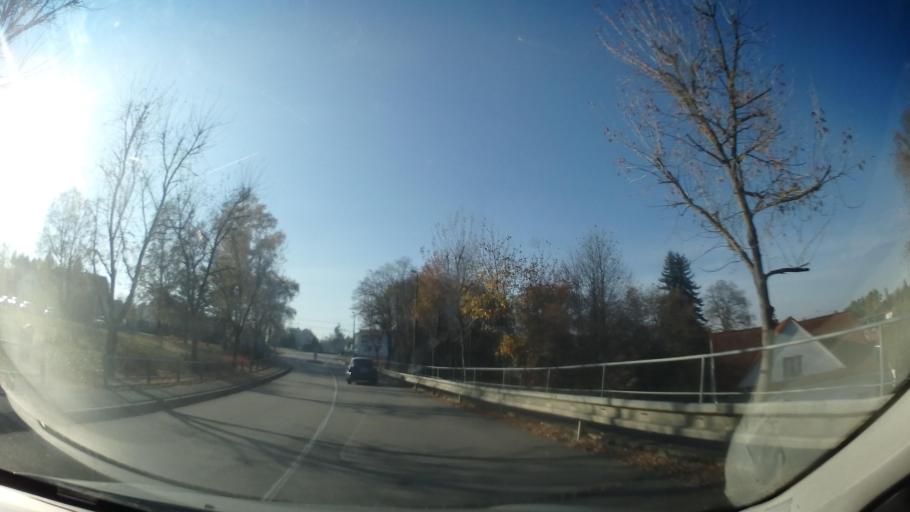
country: CZ
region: Central Bohemia
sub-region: Okres Praha-Vychod
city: Mnichovice
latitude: 49.9099
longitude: 14.7125
